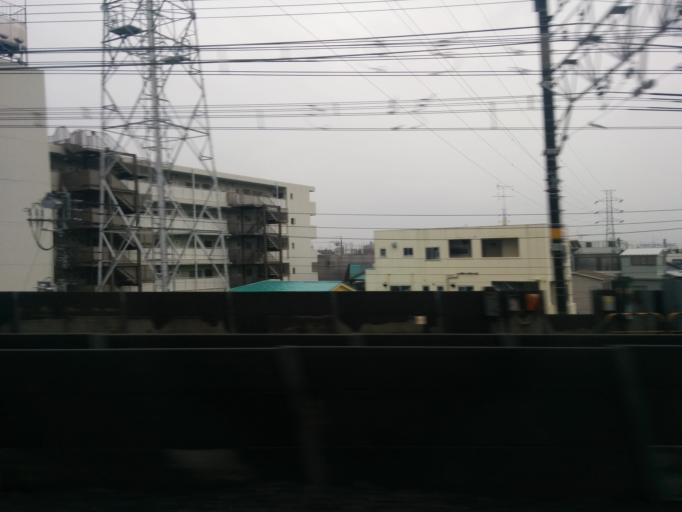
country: JP
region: Chiba
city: Matsudo
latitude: 35.7302
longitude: 139.8774
